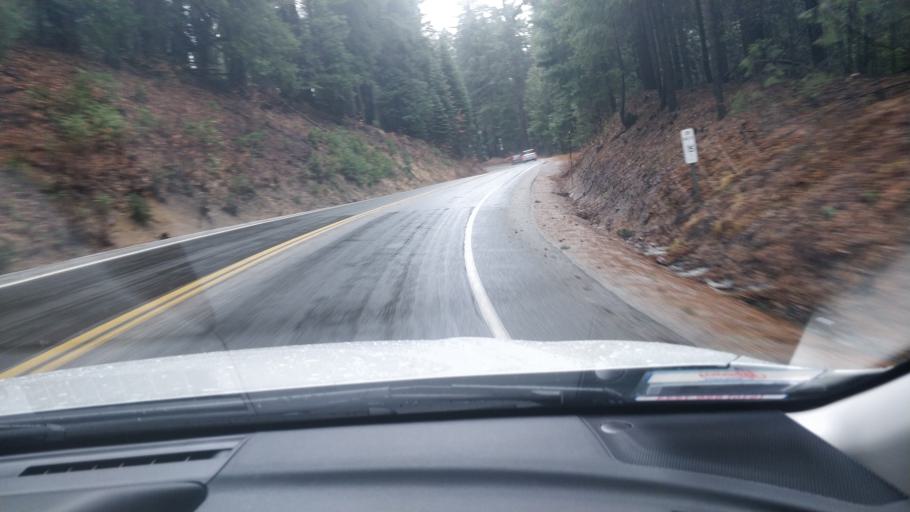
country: US
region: California
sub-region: Nevada County
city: Nevada City
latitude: 39.3238
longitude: -120.8318
